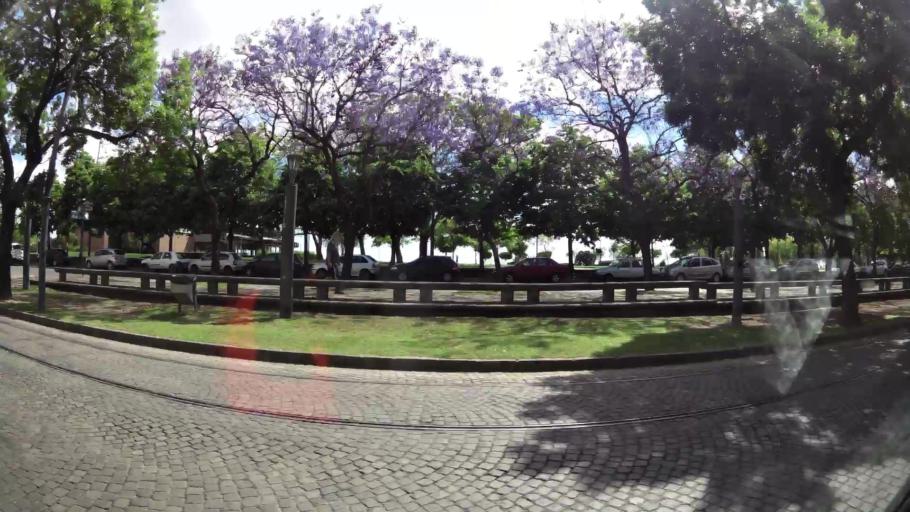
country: AR
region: Santa Fe
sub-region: Departamento de Rosario
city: Rosario
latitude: -32.9337
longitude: -60.6462
